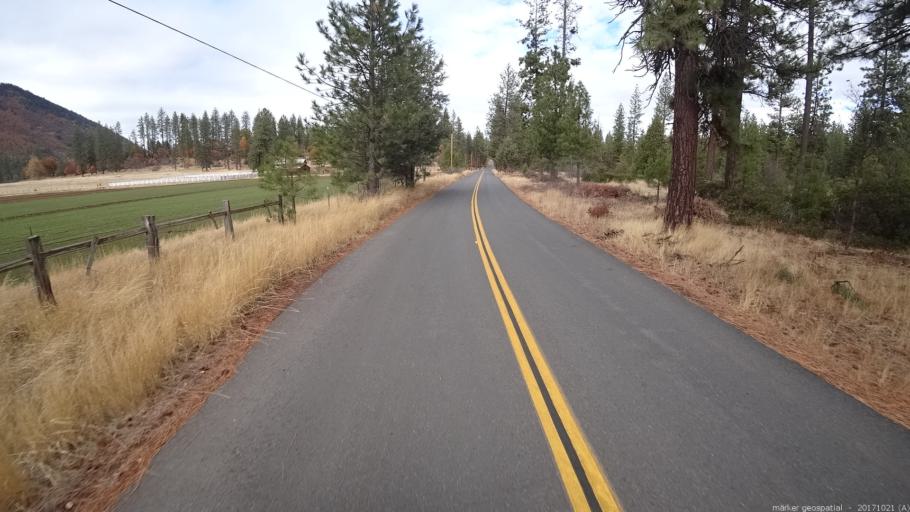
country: US
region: California
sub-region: Shasta County
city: Burney
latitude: 40.9420
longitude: -121.6457
